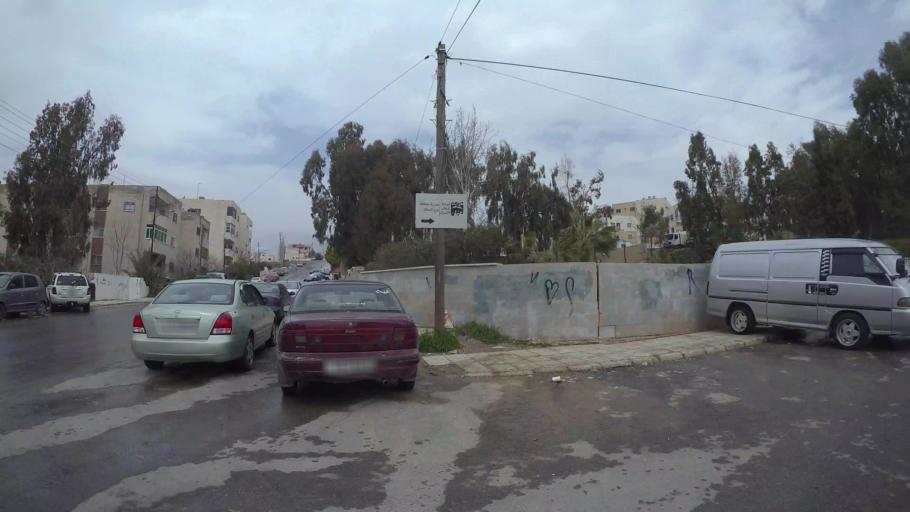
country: JO
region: Amman
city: Umm as Summaq
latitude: 31.9023
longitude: 35.8385
